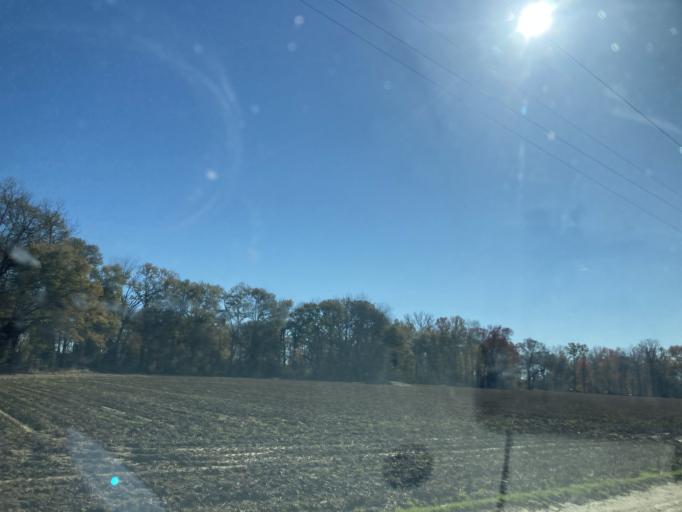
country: US
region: Mississippi
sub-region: Sharkey County
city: Rolling Fork
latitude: 32.8190
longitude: -90.7302
